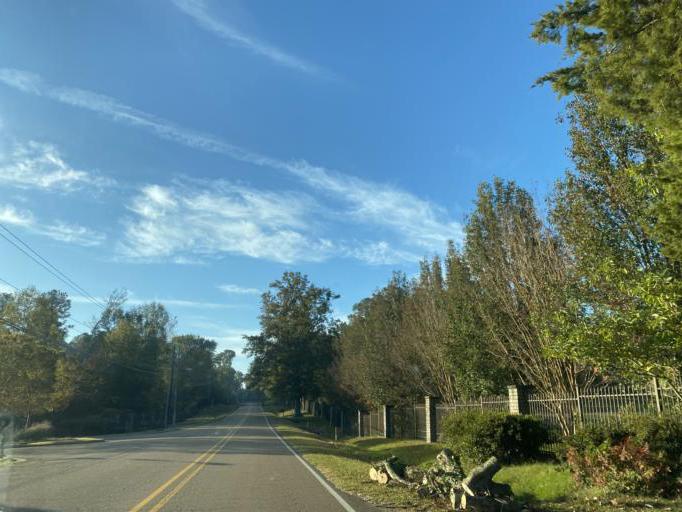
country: US
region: Mississippi
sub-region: Madison County
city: Madison
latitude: 32.4697
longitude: -90.0721
